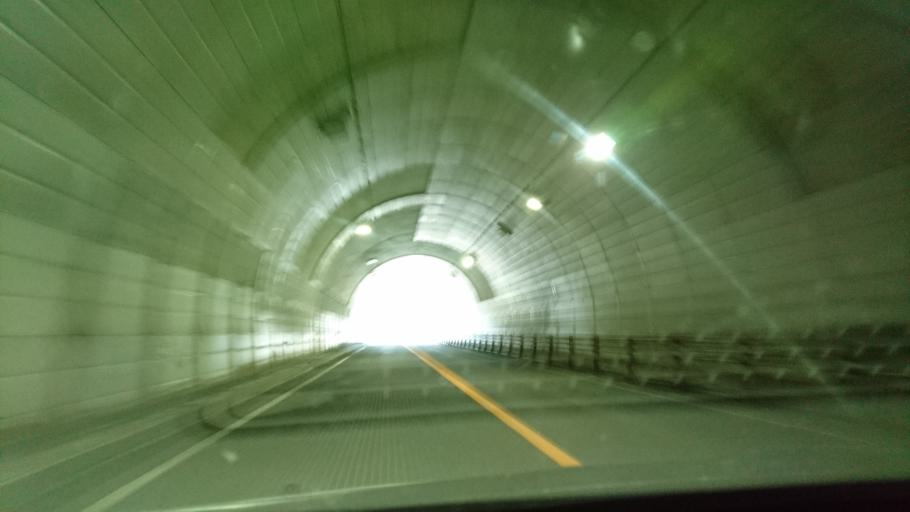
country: JP
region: Akita
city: Omagari
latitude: 39.3127
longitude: 140.2632
